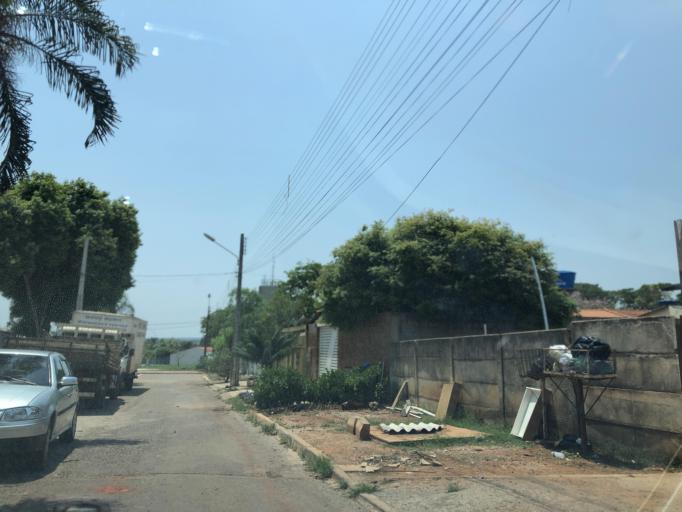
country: BR
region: Federal District
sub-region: Brasilia
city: Brasilia
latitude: -15.9344
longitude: -47.9417
